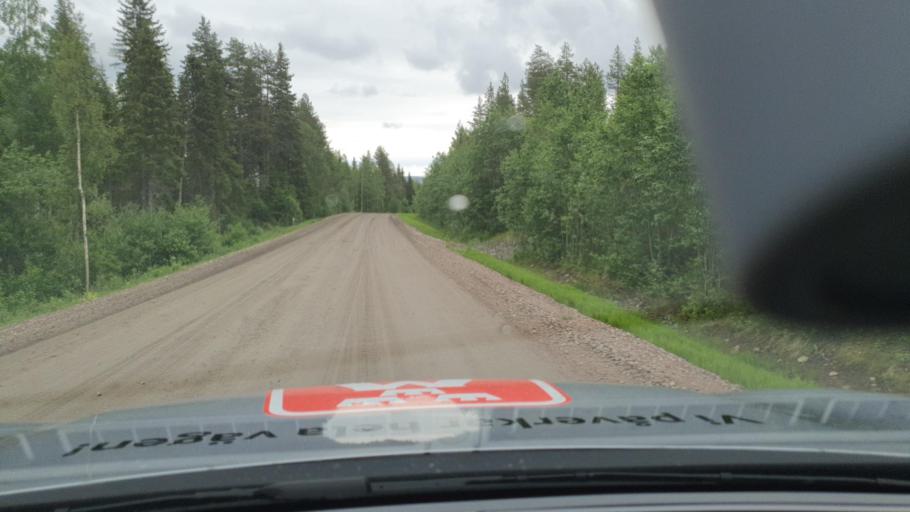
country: SE
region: Norrbotten
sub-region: Overtornea Kommun
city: OEvertornea
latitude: 66.4195
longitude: 23.5721
